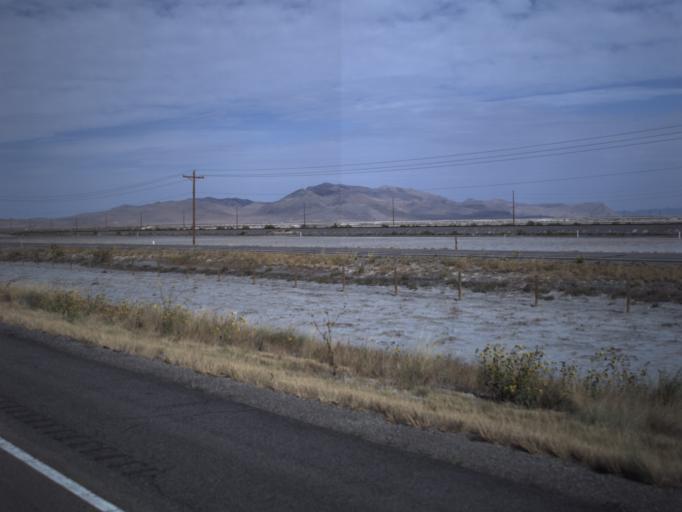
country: US
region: Utah
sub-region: Tooele County
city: Grantsville
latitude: 40.7471
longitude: -112.6625
